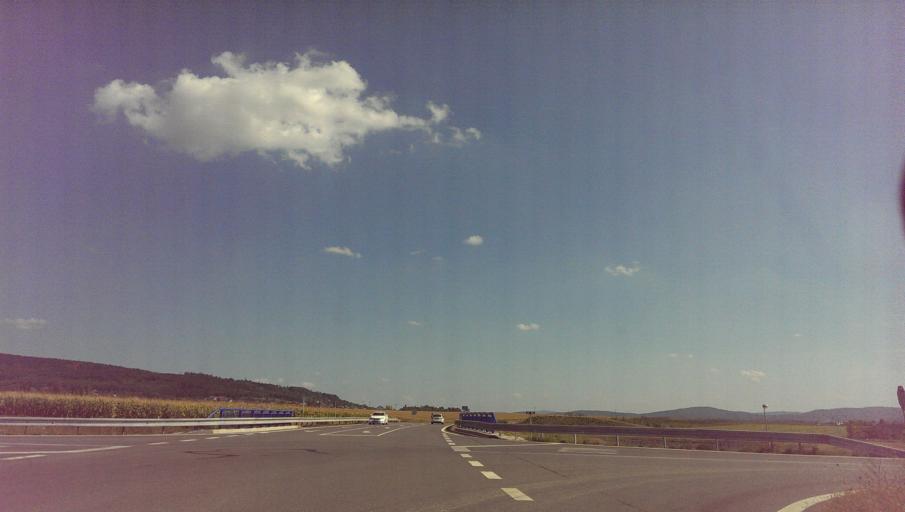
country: CZ
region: Zlin
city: Holesov
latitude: 49.3329
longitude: 17.5945
